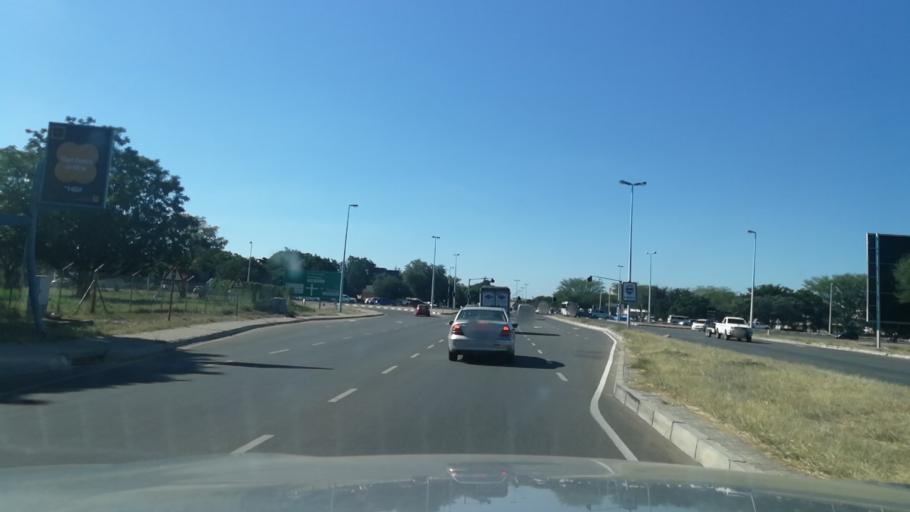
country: BW
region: South East
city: Gaborone
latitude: -24.6736
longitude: 25.9233
